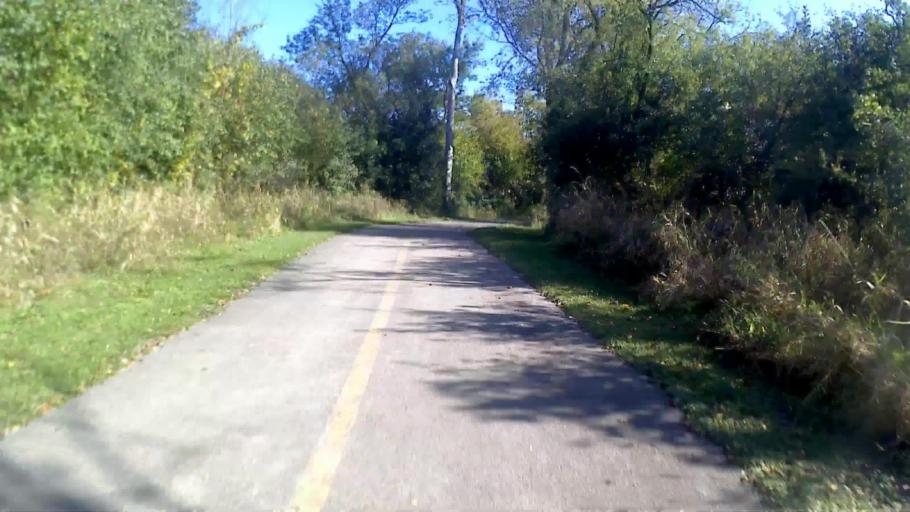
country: US
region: Illinois
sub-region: DuPage County
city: Addison
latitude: 41.9374
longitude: -87.9851
